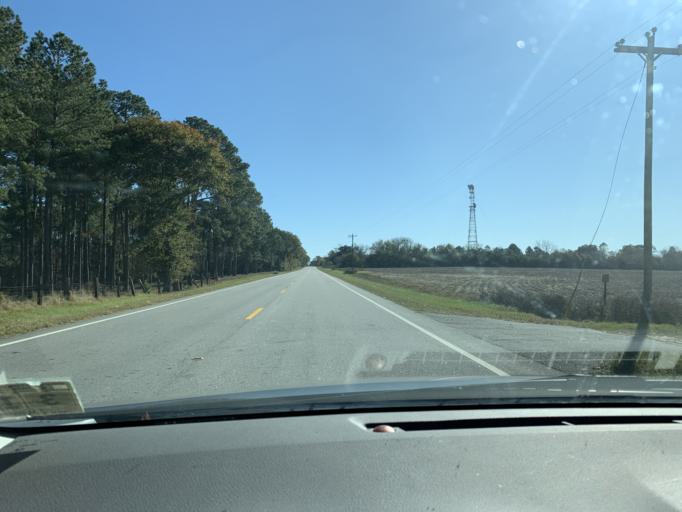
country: US
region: Georgia
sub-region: Ben Hill County
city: Fitzgerald
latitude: 31.7078
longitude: -83.1630
